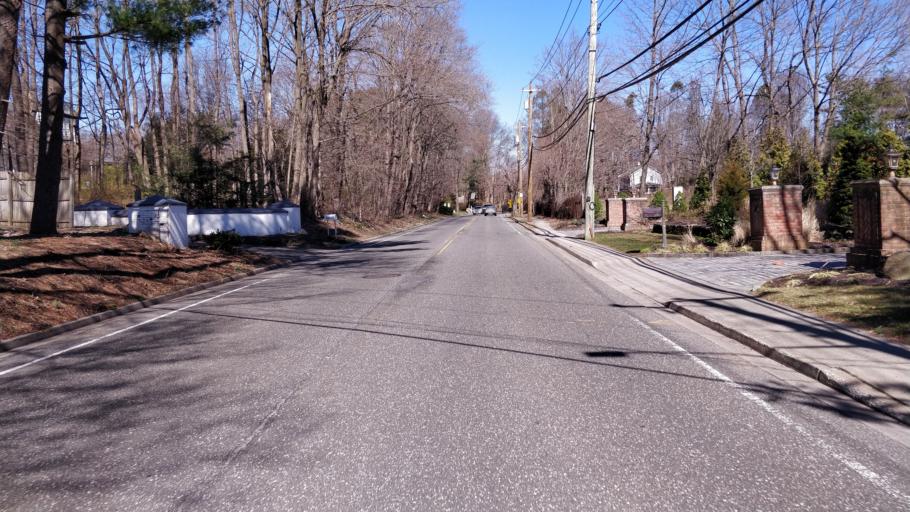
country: US
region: New York
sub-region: Nassau County
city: Syosset
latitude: 40.8387
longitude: -73.5145
